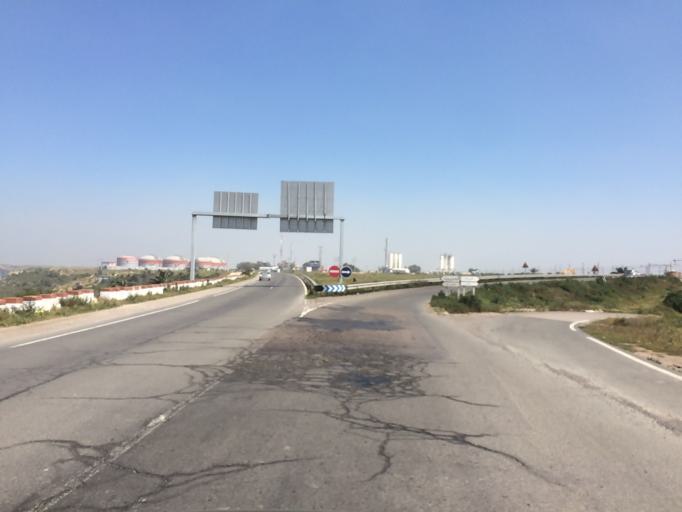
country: MA
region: Doukkala-Abda
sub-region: El-Jadida
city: Moulay Abdallah
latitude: 33.1345
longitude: -8.6100
